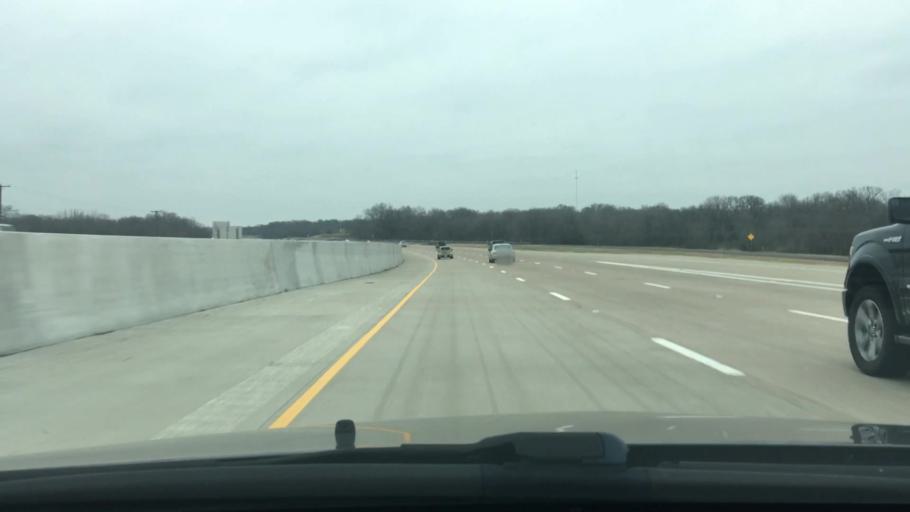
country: US
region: Texas
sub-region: Freestone County
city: Wortham
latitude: 31.9239
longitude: -96.4139
